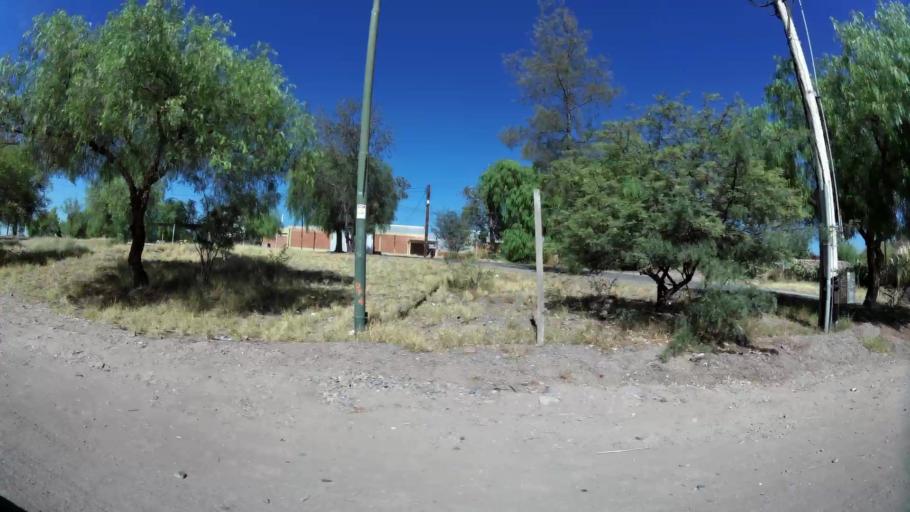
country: AR
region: Mendoza
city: Mendoza
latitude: -32.8934
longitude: -68.8841
